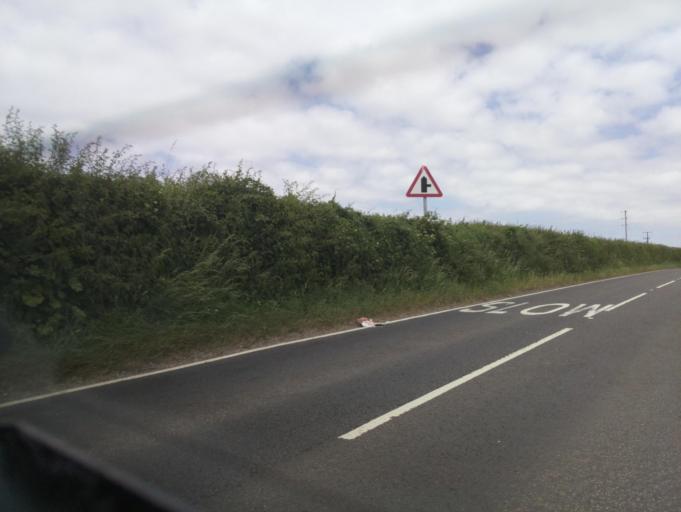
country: GB
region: England
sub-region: Dorset
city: Sherborne
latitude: 50.9630
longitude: -2.5160
